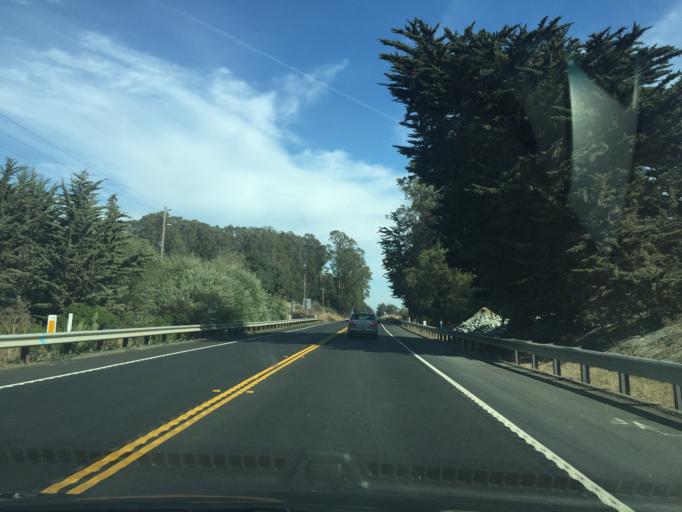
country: US
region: California
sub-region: Santa Cruz County
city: Santa Cruz
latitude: 36.9621
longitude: -122.0718
